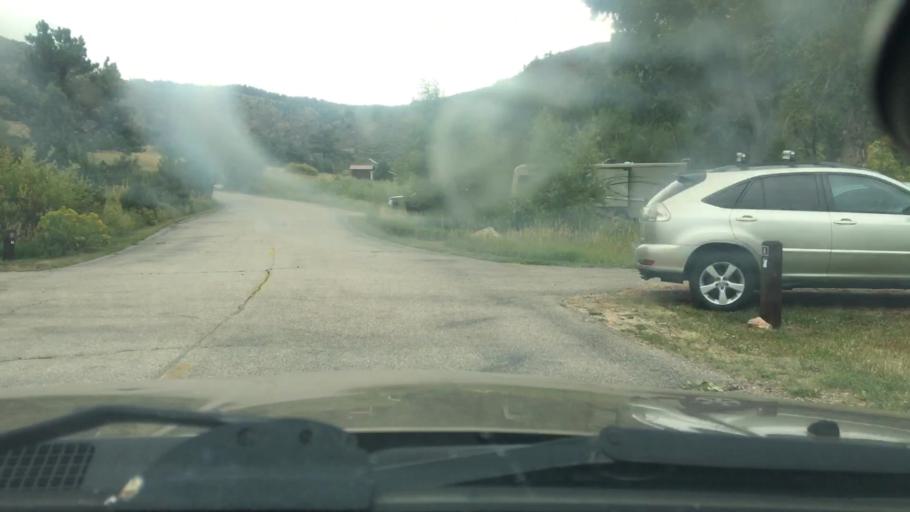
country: US
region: Colorado
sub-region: Larimer County
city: Laporte
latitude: 40.6952
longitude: -105.4463
